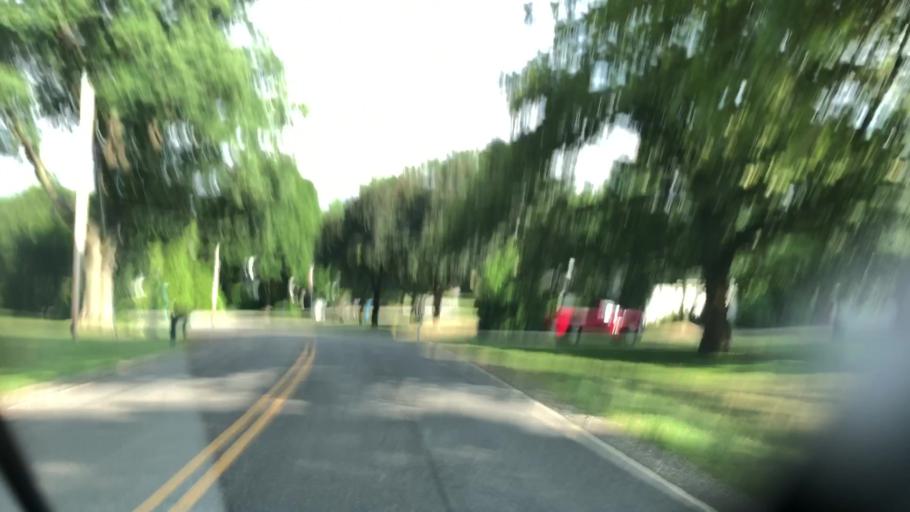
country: US
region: Ohio
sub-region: Summit County
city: Norton
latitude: 41.0215
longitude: -81.6318
